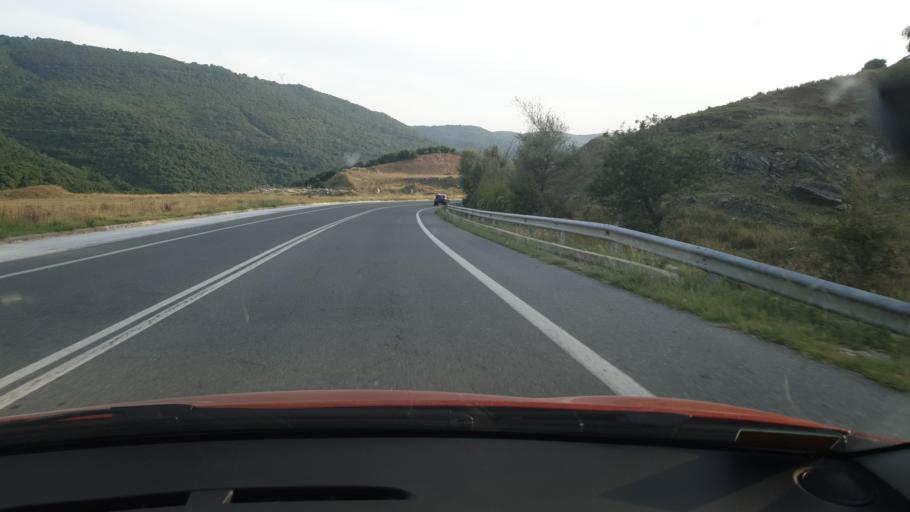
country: GR
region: Central Macedonia
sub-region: Nomos Chalkidikis
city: Galatista
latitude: 40.4594
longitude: 23.3224
